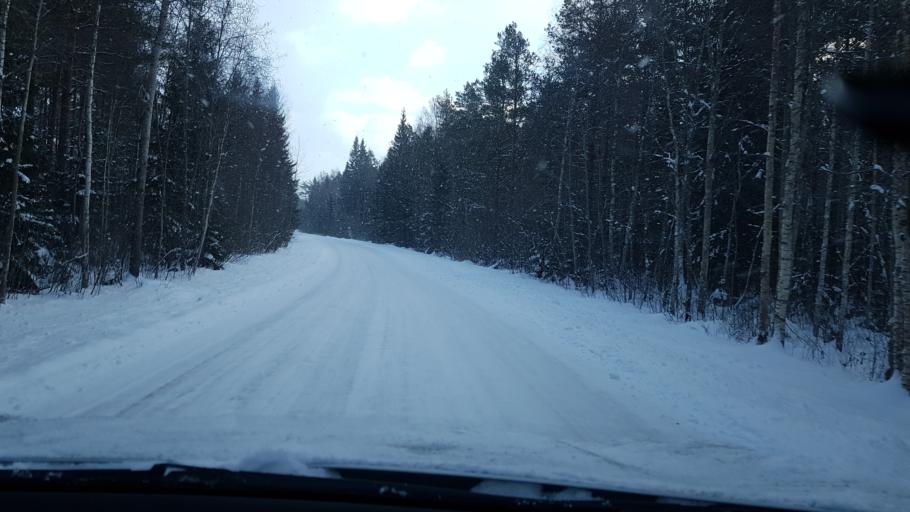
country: EE
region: Harju
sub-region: Nissi vald
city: Turba
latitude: 59.1735
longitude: 24.1337
